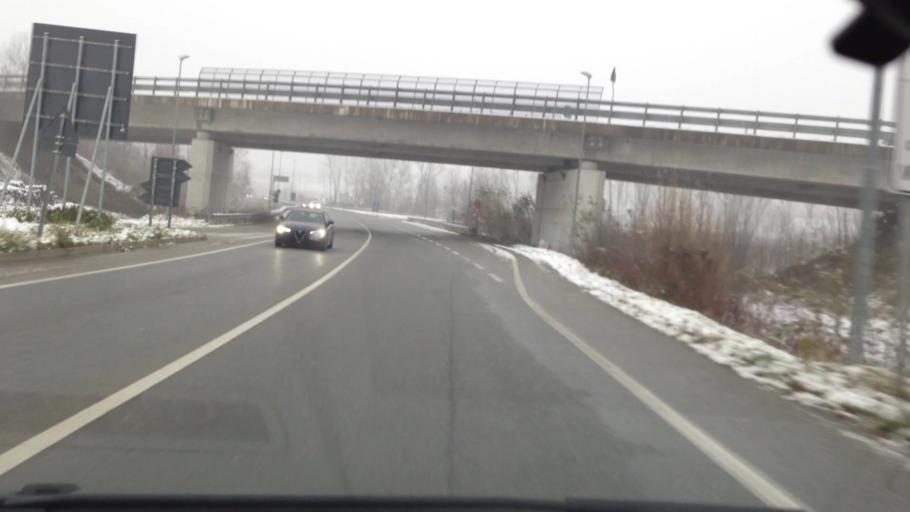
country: IT
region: Piedmont
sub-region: Provincia di Asti
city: Piano-Molini d'Isola
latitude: 44.8302
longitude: 8.2032
